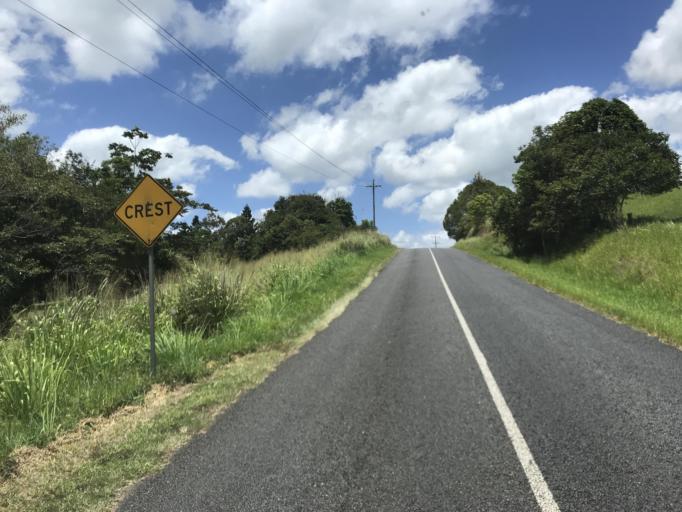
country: AU
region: Queensland
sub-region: Tablelands
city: Atherton
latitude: -17.3439
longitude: 145.5933
